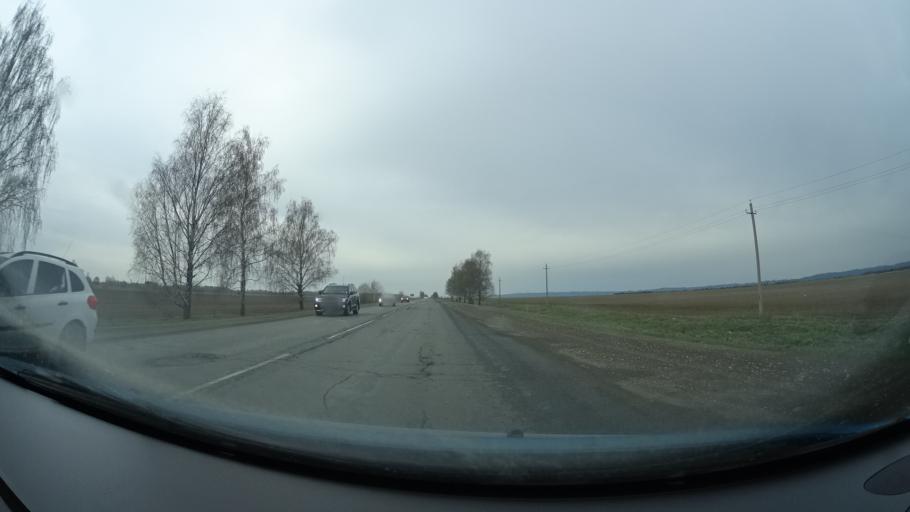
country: RU
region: Perm
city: Ust'-Kachka
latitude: 58.0675
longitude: 55.6260
